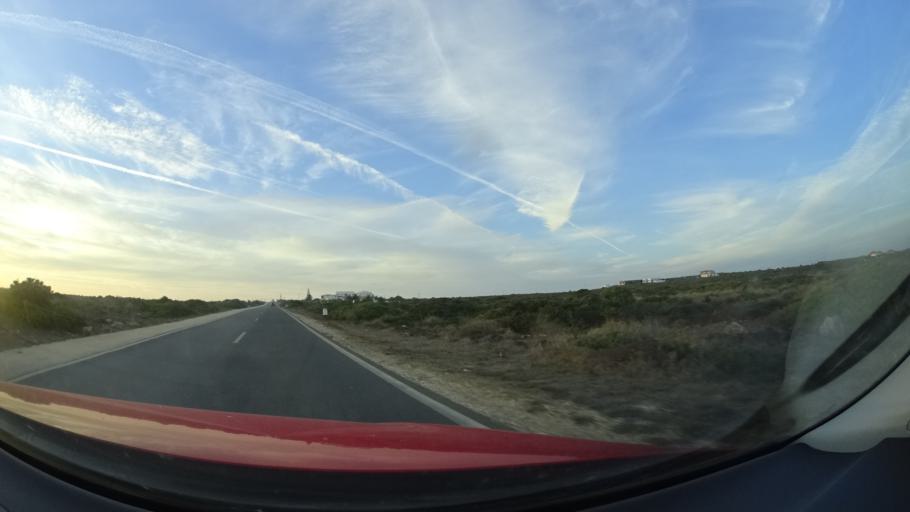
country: PT
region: Faro
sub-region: Vila do Bispo
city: Sagres
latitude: 37.0232
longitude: -8.9607
